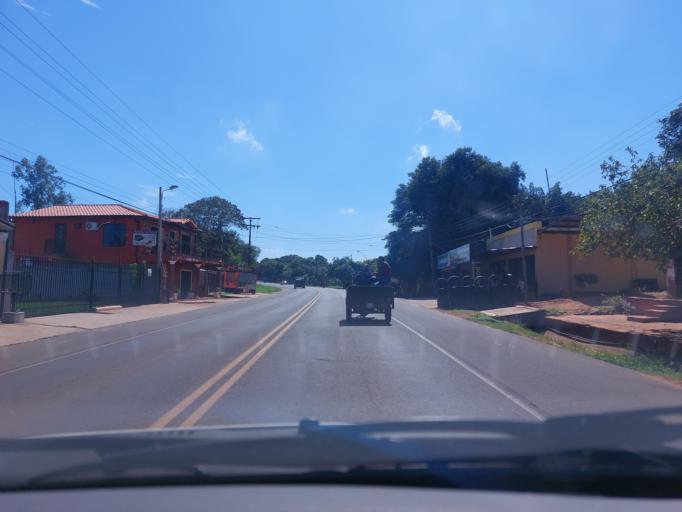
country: PY
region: San Pedro
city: Guayaybi
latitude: -24.6662
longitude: -56.4559
